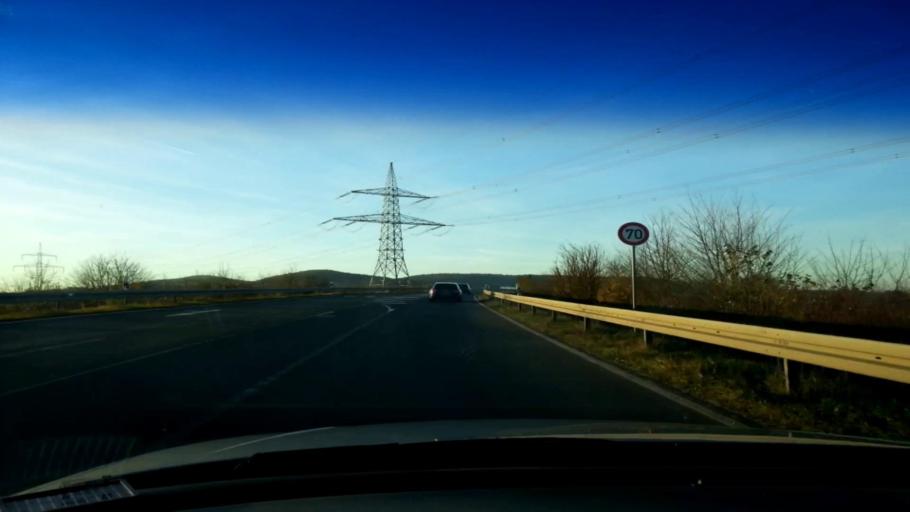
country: DE
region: Bavaria
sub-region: Upper Franconia
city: Hallstadt
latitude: 49.9346
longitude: 10.8879
